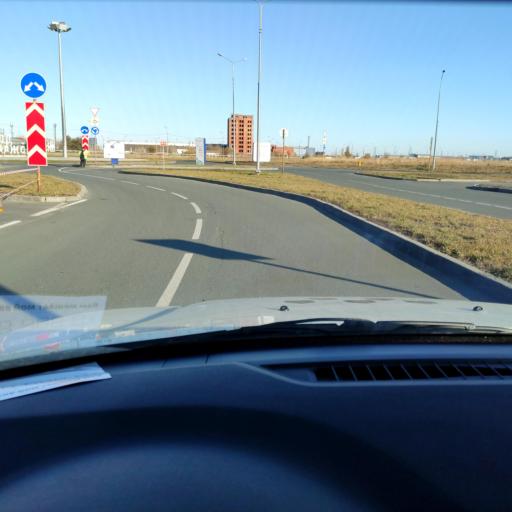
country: RU
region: Samara
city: Tol'yatti
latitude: 53.5518
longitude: 49.3428
